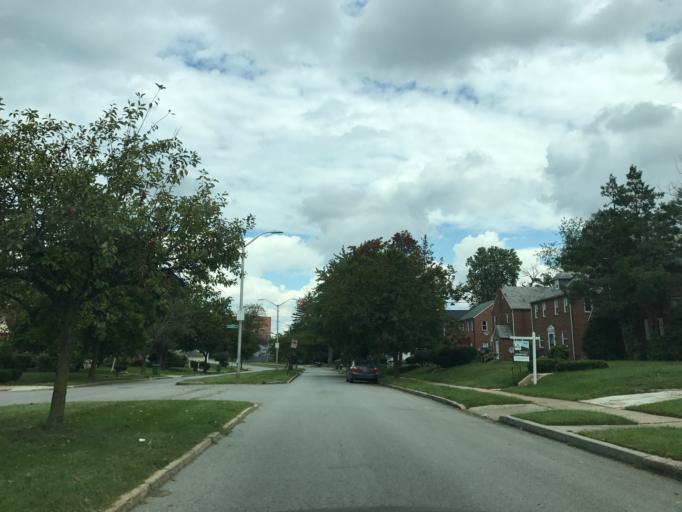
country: US
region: Maryland
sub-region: Baltimore County
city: Lochearn
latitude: 39.3317
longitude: -76.6761
